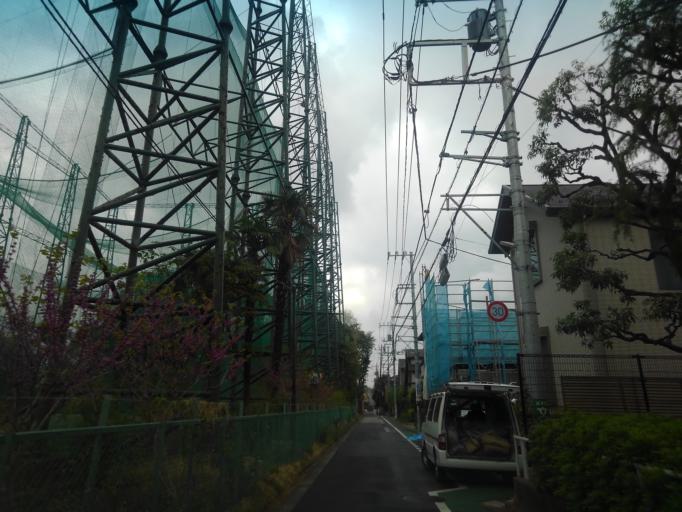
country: JP
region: Tokyo
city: Musashino
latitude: 35.7203
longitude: 139.5866
